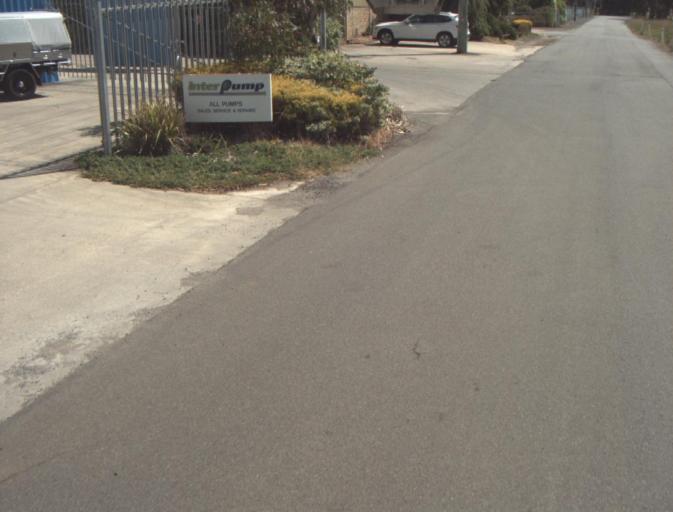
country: AU
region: Tasmania
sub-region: Launceston
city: Launceston
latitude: -41.4199
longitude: 147.1425
